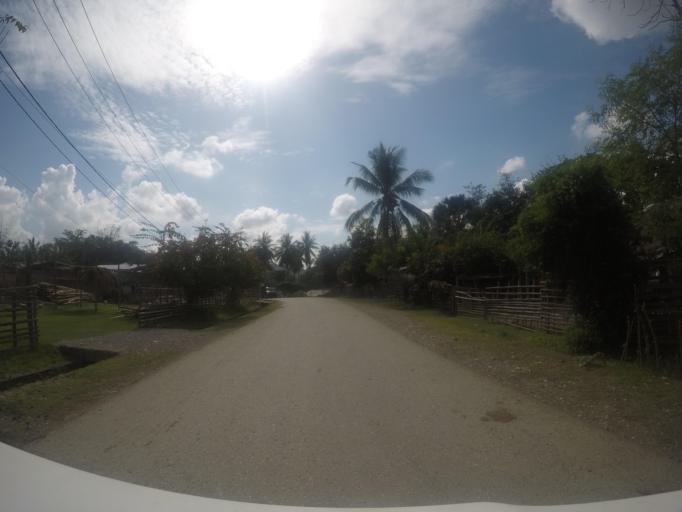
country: TL
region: Viqueque
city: Viqueque
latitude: -8.8541
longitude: 126.3599
